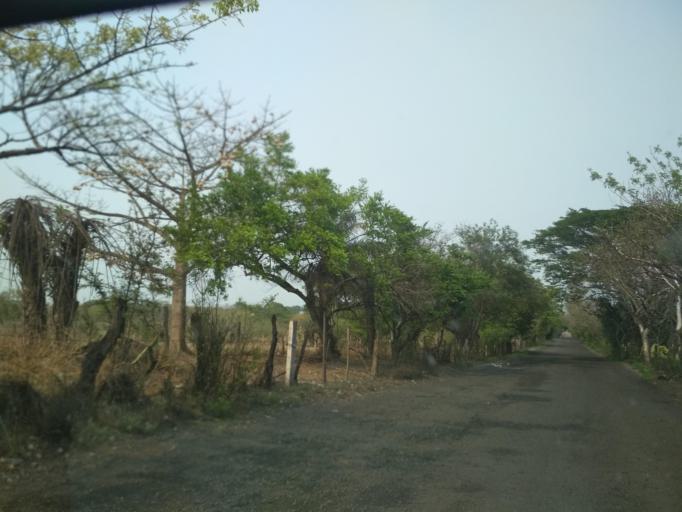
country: MX
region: Veracruz
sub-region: Veracruz
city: Delfino Victoria (Santa Fe)
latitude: 19.1567
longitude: -96.2674
